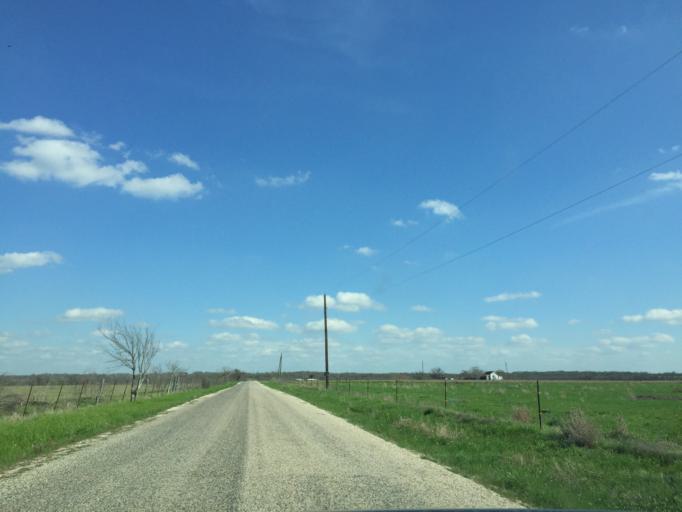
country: US
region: Texas
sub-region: Milam County
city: Thorndale
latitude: 30.5977
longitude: -97.1727
